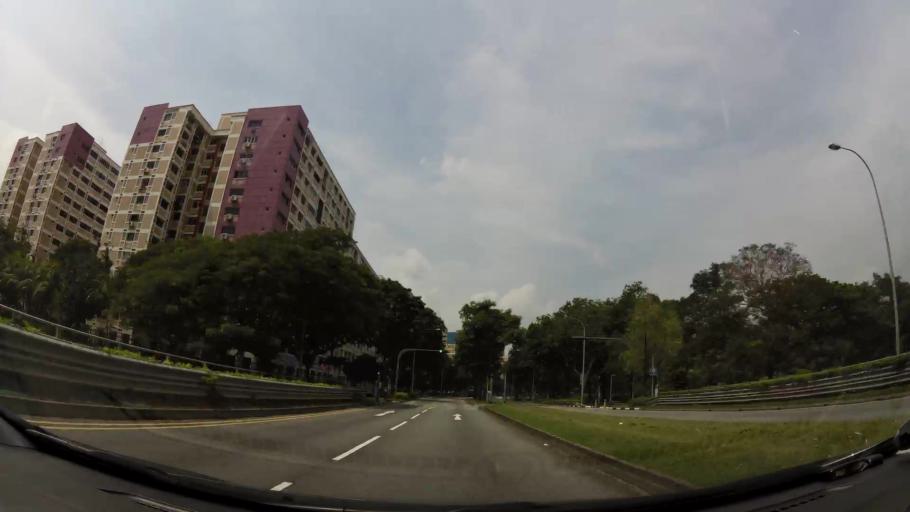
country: MY
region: Johor
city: Kampung Pasir Gudang Baru
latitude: 1.3692
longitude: 103.9543
